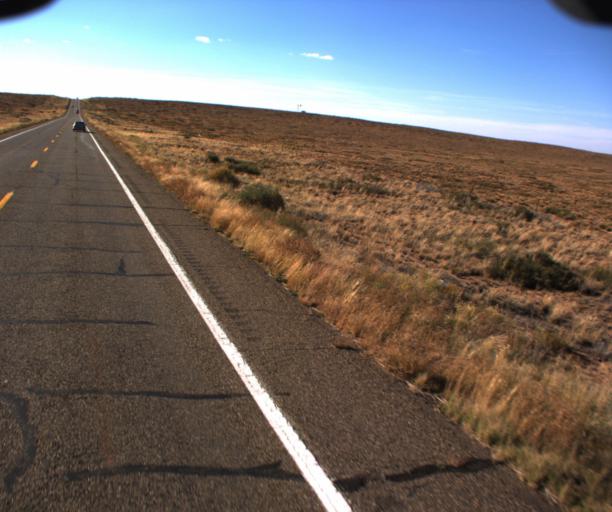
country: US
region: Arizona
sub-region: Coconino County
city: Kaibito
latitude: 36.6122
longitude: -111.0223
